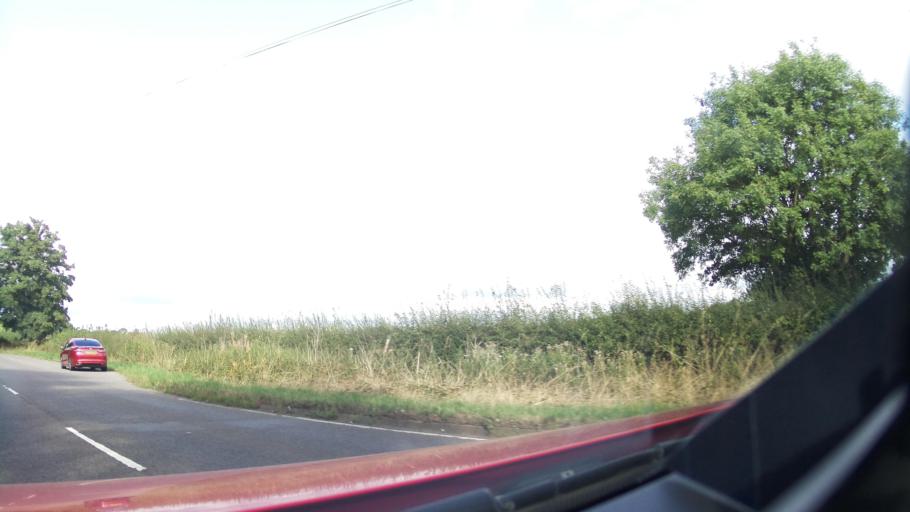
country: GB
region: England
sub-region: Leicestershire
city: Ashby de la Zouch
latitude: 52.7290
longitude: -1.4874
